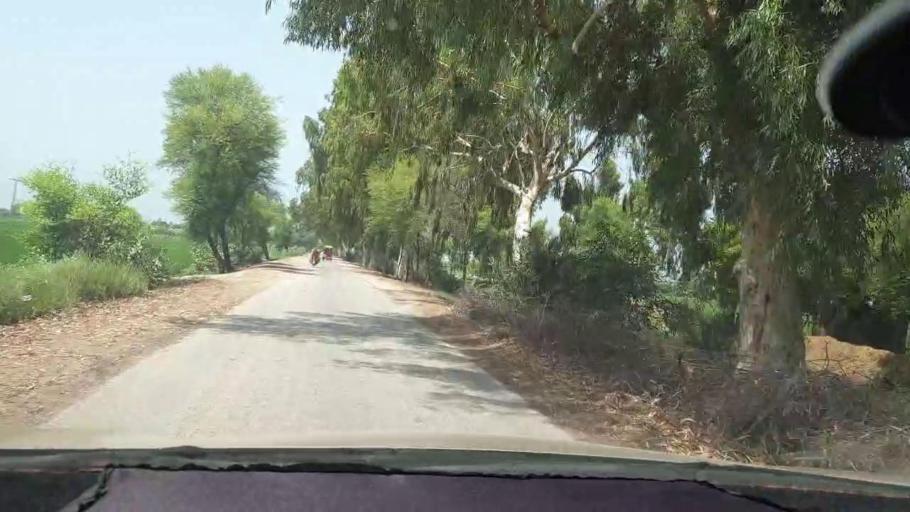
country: PK
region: Sindh
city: Kambar
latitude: 27.6336
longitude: 67.9880
